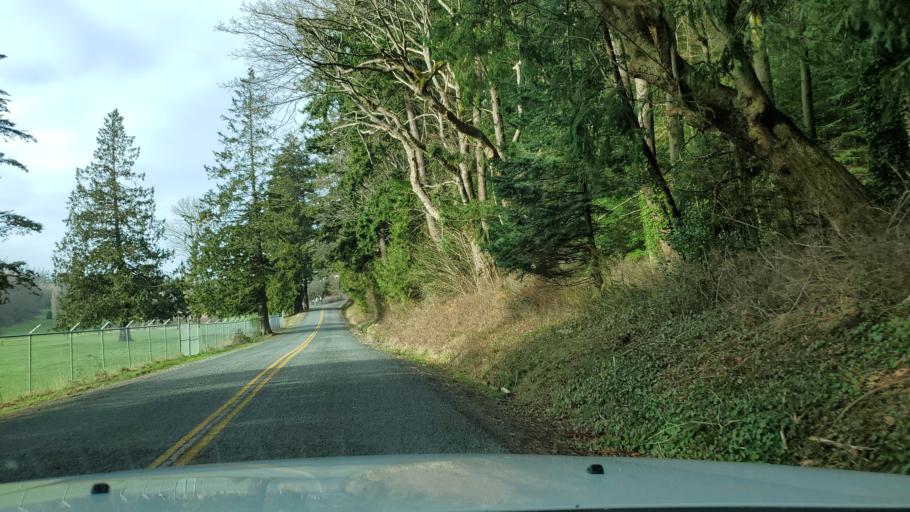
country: US
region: Washington
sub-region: Skagit County
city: Anacortes
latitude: 48.4514
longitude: -122.5744
